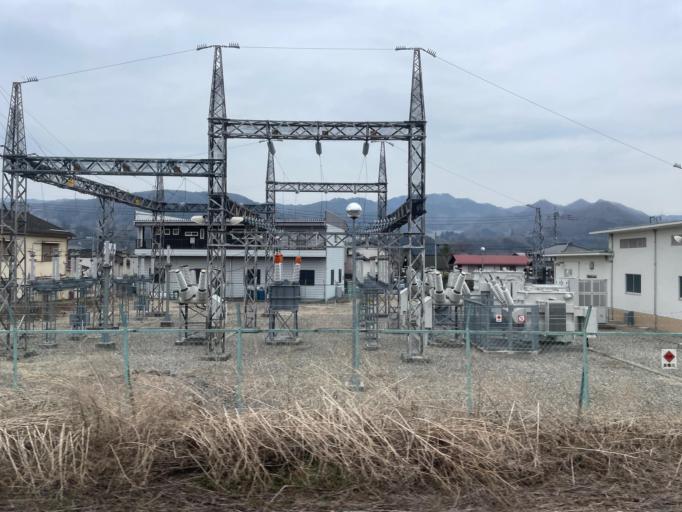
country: JP
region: Gunma
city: Numata
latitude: 36.6506
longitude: 139.0301
